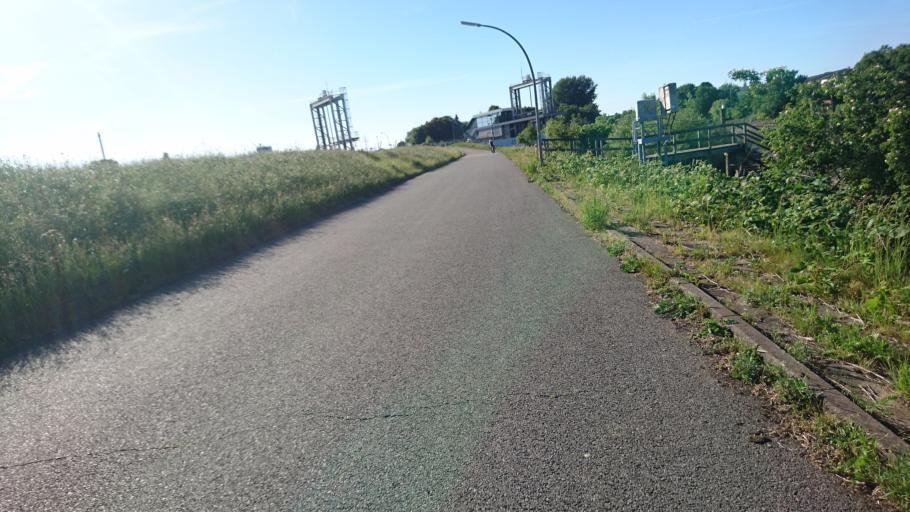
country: DE
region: Hamburg
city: Kleiner Grasbrook
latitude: 53.5217
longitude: 9.9851
